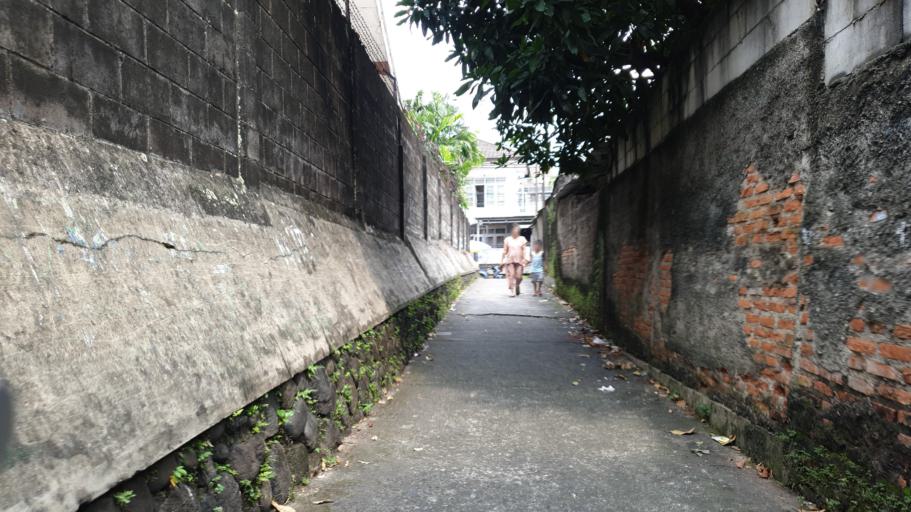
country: ID
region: Banten
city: South Tangerang
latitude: -6.2858
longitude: 106.7928
